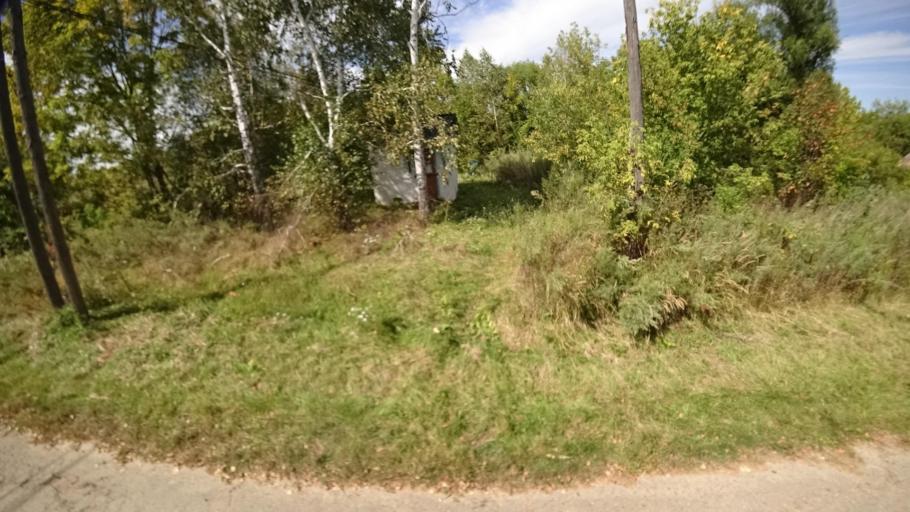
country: RU
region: Primorskiy
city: Yakovlevka
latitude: 44.6563
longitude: 133.7449
